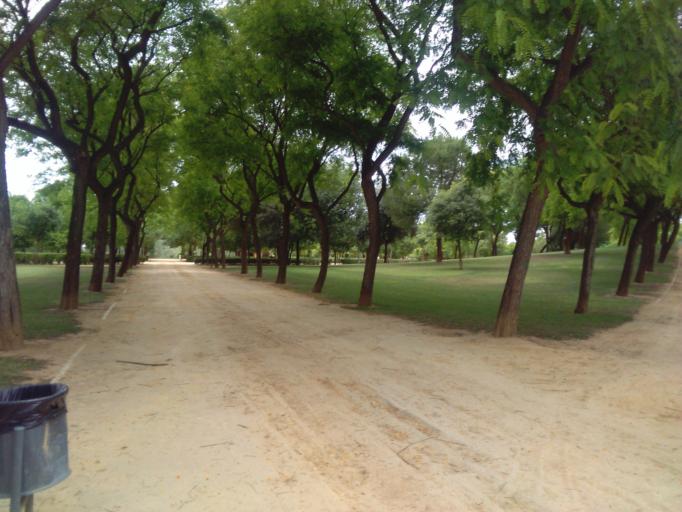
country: ES
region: Andalusia
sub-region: Provincia de Sevilla
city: La Algaba
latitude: 37.4269
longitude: -5.9898
